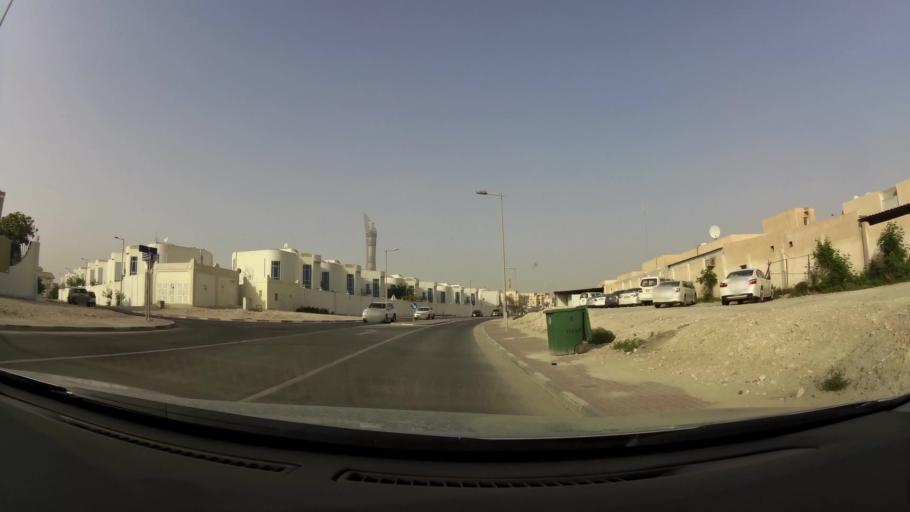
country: QA
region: Baladiyat ar Rayyan
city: Ar Rayyan
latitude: 25.2525
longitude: 51.4385
